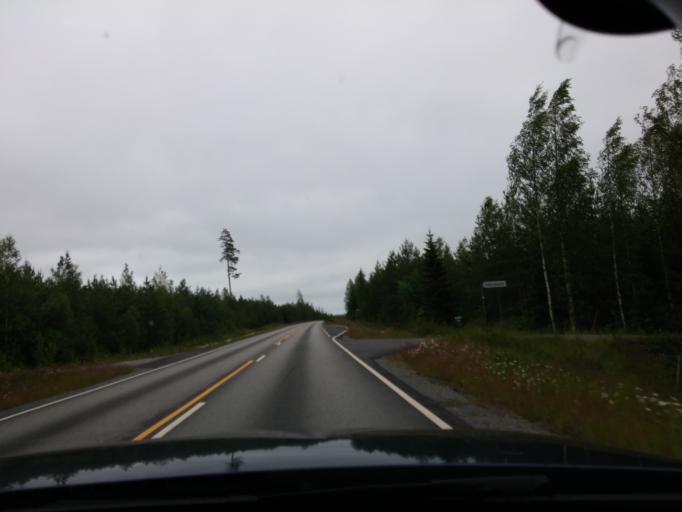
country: FI
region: Central Finland
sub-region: Saarijaervi-Viitasaari
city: Saarijaervi
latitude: 62.6795
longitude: 25.1840
